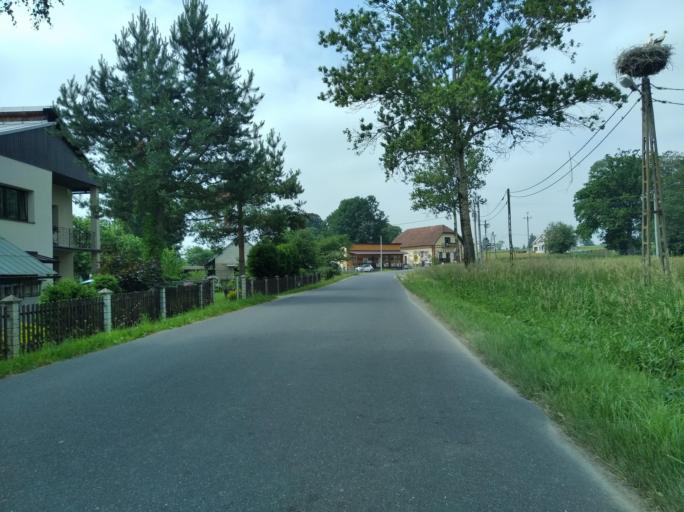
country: PL
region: Subcarpathian Voivodeship
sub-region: Powiat brzozowski
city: Haczow
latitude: 49.6305
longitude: 21.9207
